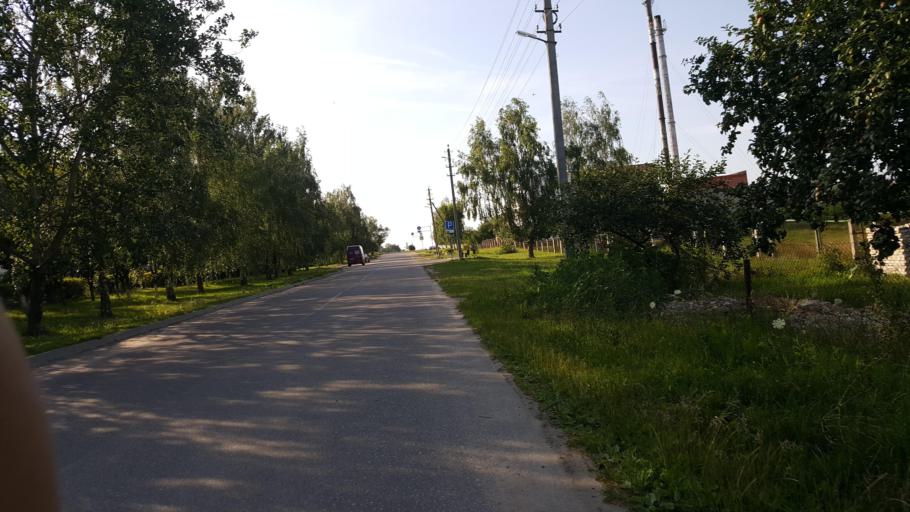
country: BY
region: Brest
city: Vysokaye
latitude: 52.3764
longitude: 23.3617
